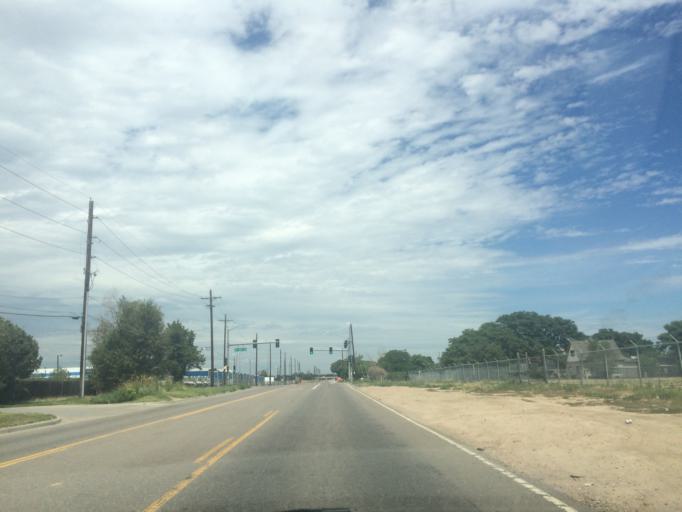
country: US
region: Colorado
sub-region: Adams County
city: Welby
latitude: 39.8154
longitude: -104.9592
